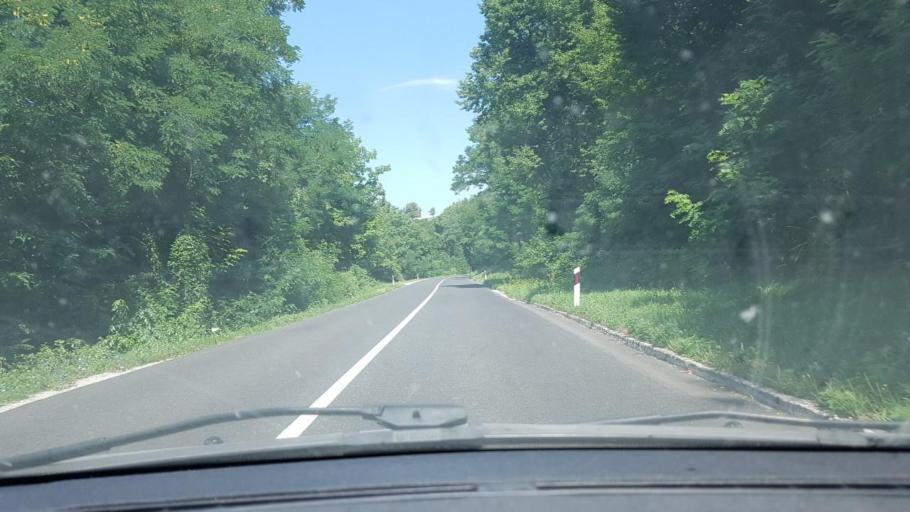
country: HR
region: Karlovacka
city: Vojnic
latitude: 45.2463
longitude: 15.7188
